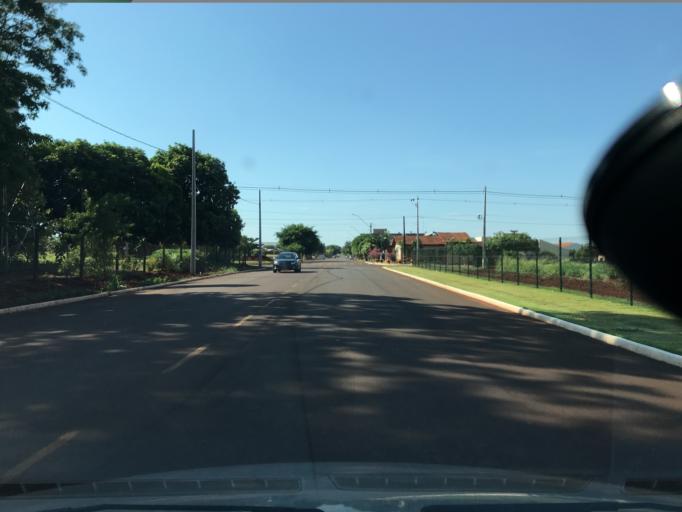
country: BR
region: Parana
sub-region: Palotina
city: Palotina
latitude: -24.2964
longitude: -53.8394
